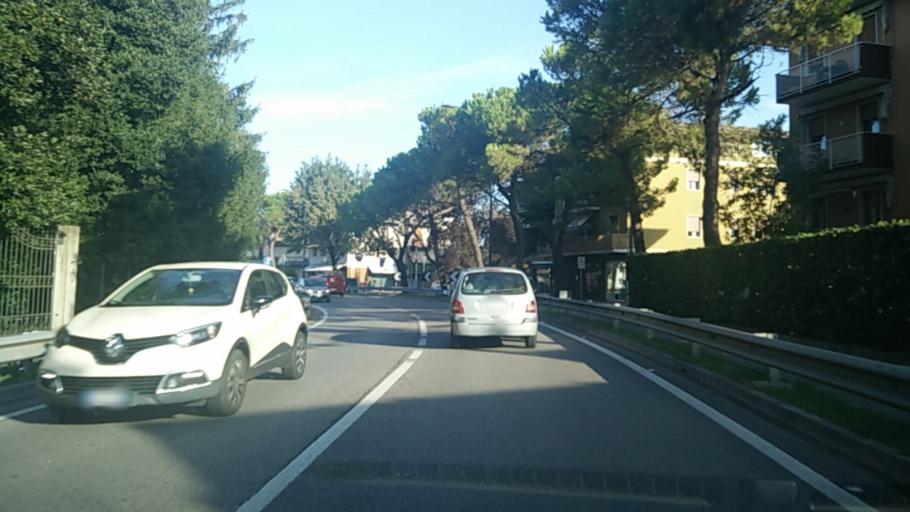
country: IT
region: Veneto
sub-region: Provincia di Venezia
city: Trivignano
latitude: 45.5279
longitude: 12.1898
